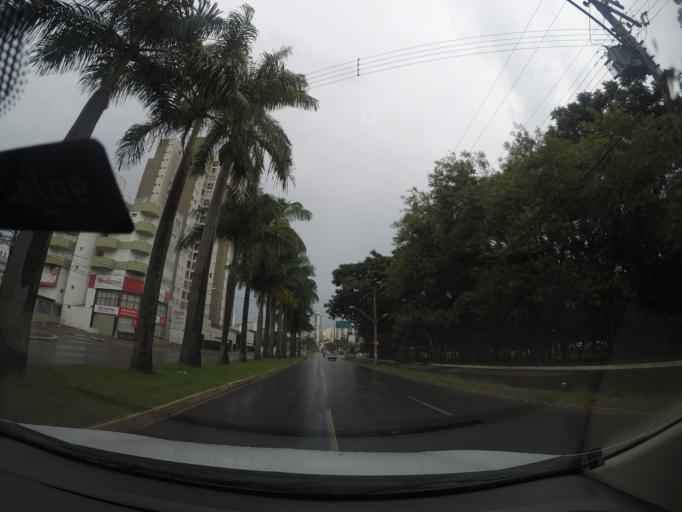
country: BR
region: Goias
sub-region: Goiania
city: Goiania
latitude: -16.7099
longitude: -49.2595
